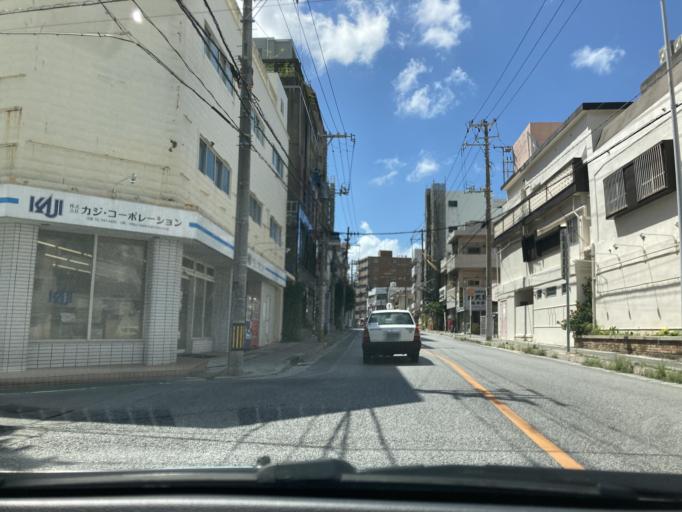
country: JP
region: Okinawa
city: Naha-shi
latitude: 26.2177
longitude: 127.6729
